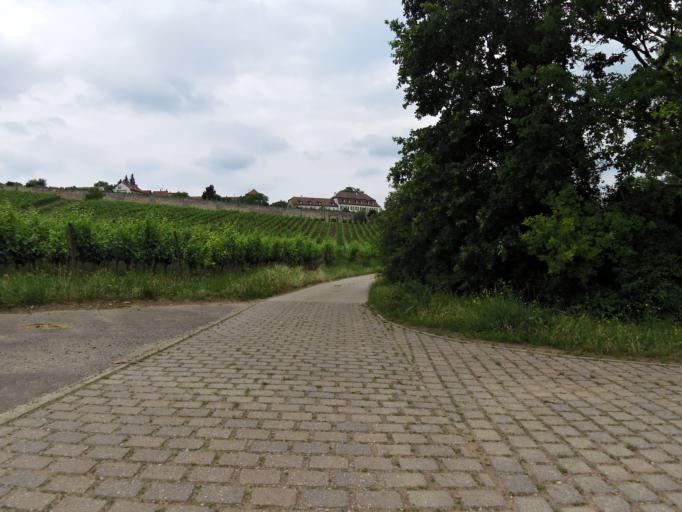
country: DE
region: Rheinland-Pfalz
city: Herxheim am Berg
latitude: 49.5058
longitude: 8.1830
